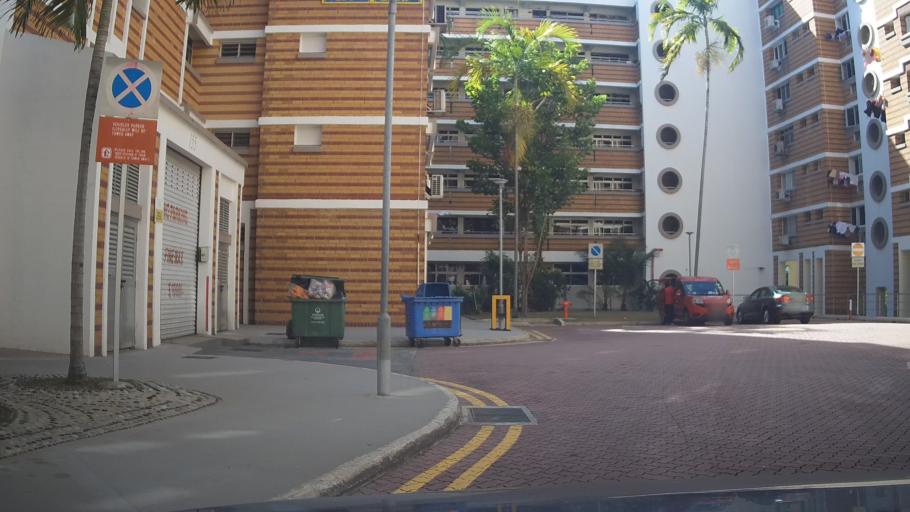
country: SG
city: Singapore
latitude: 1.3639
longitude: 103.9631
